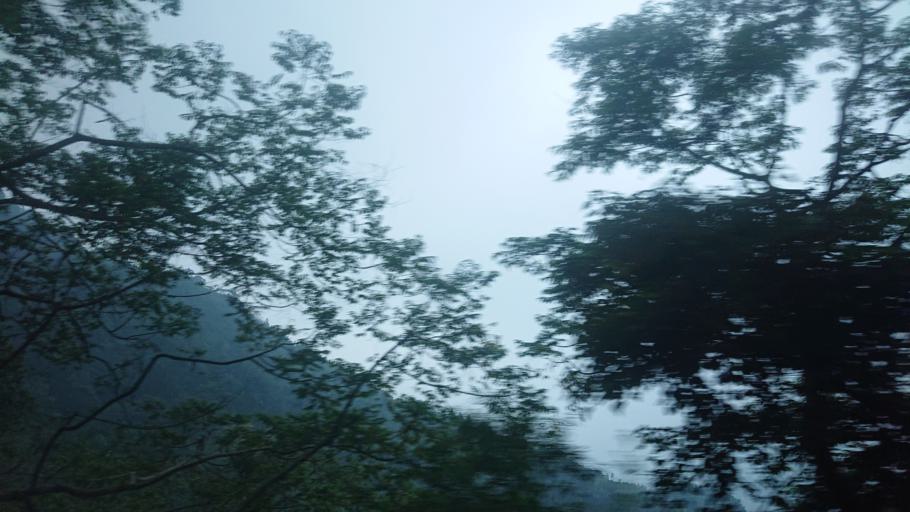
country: TW
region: Taiwan
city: Lugu
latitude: 23.5887
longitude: 120.7252
